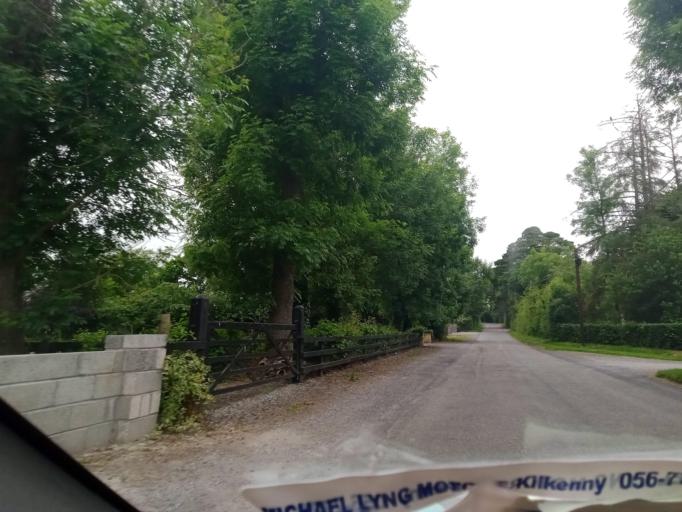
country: IE
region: Leinster
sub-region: Kilkenny
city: Ballyragget
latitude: 52.7404
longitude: -7.4166
